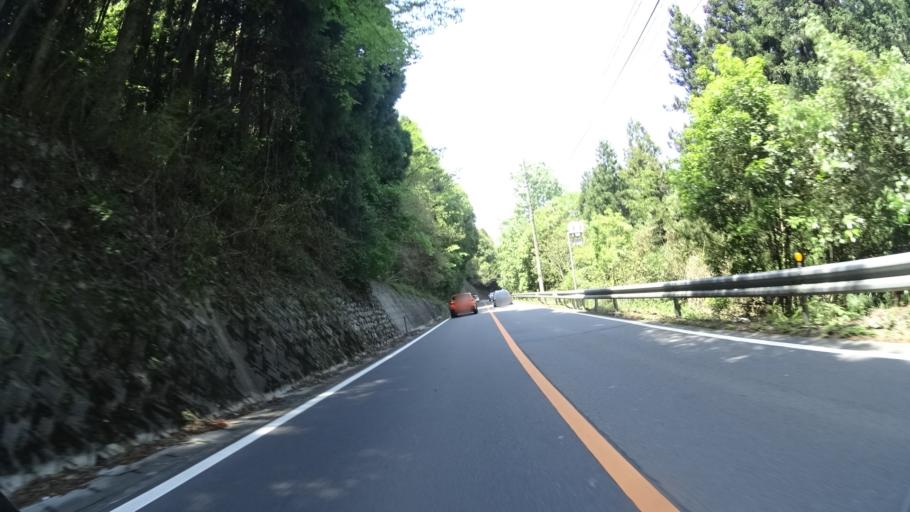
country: JP
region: Ehime
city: Hojo
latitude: 33.9723
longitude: 132.9023
